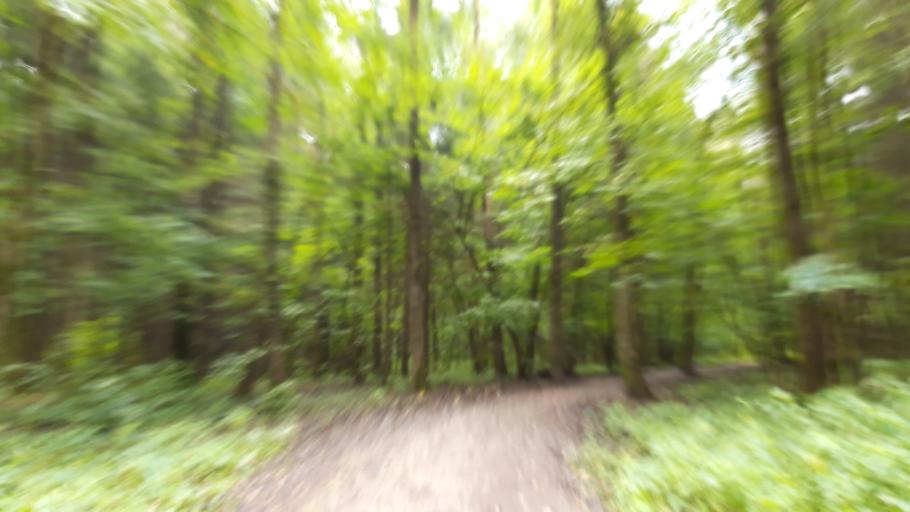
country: RU
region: Moscow
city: Zelenograd
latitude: 55.9867
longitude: 37.2040
